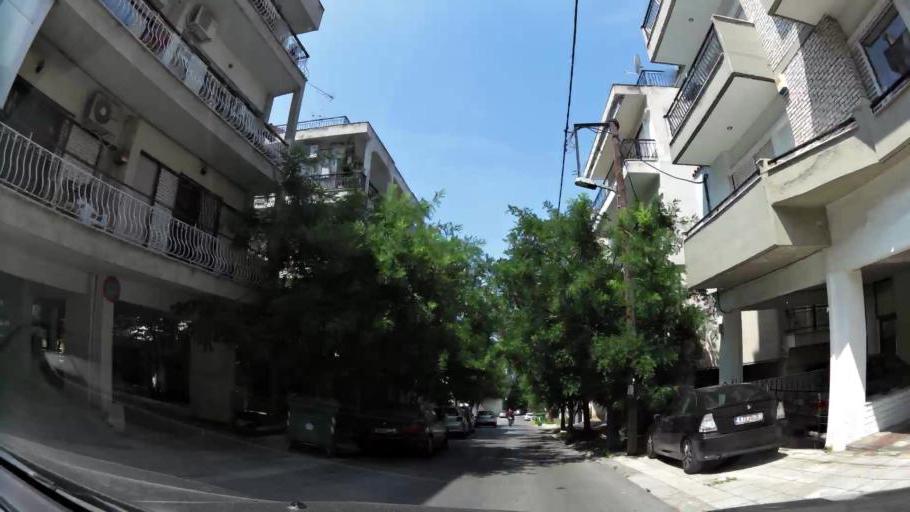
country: GR
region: Central Macedonia
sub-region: Nomos Thessalonikis
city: Agios Pavlos
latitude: 40.6335
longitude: 22.9668
